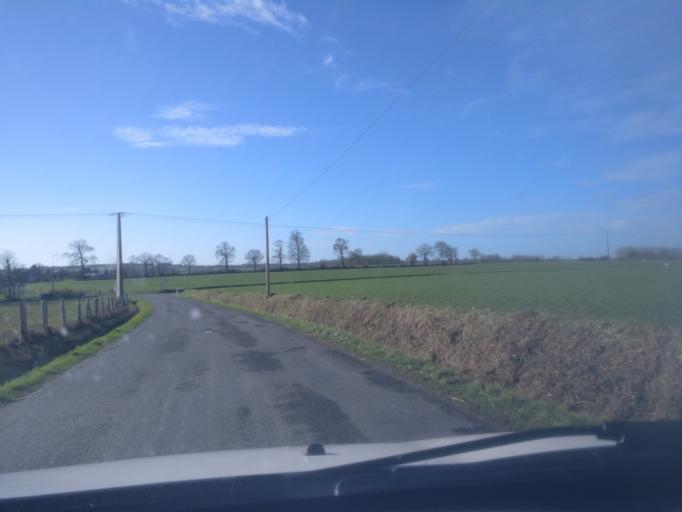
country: FR
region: Lower Normandy
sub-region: Departement de la Manche
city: Pontorson
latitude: 48.5309
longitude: -1.5240
